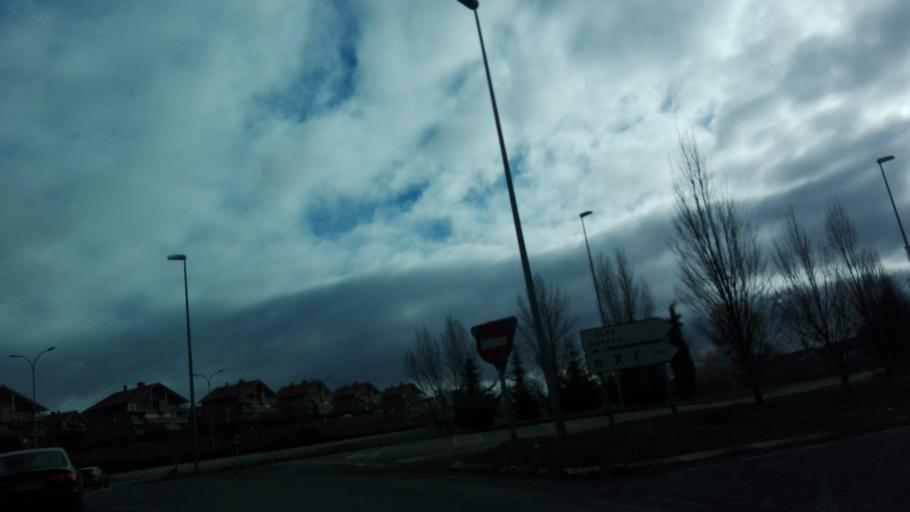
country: ES
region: Navarre
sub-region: Provincia de Navarra
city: Egues-Uharte
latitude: 42.8258
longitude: -1.5849
